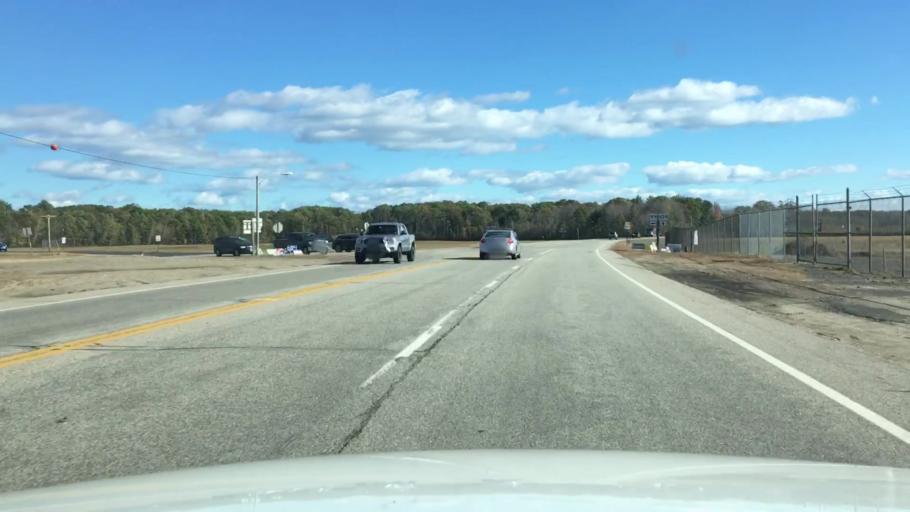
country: US
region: Maine
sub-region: York County
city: South Sanford
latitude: 43.3979
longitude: -70.6983
